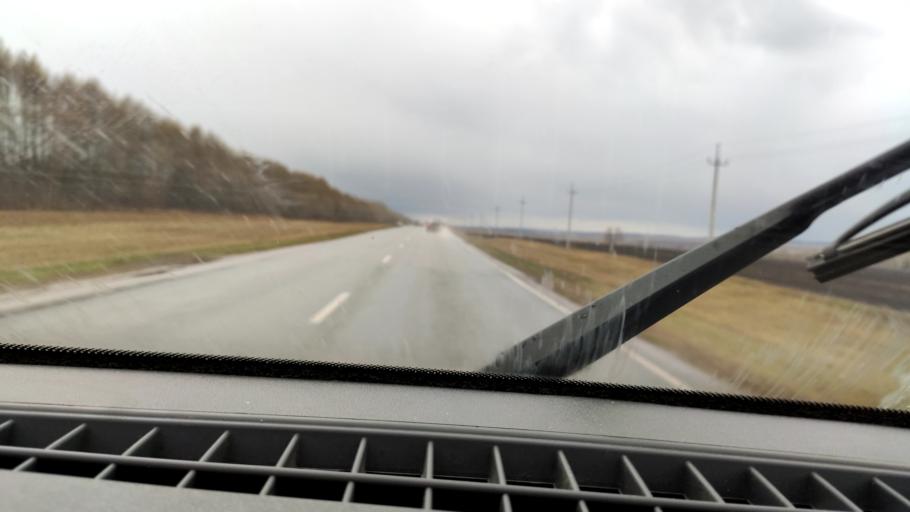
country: RU
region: Bashkortostan
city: Chekmagush
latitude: 55.1116
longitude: 54.9124
